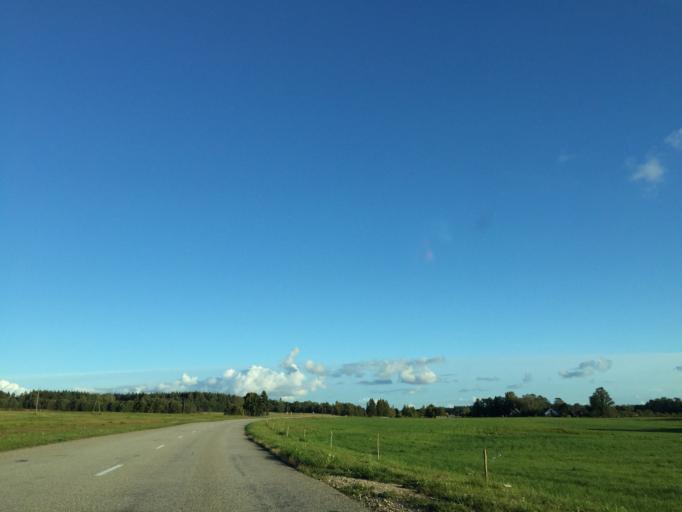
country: LV
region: Kuldigas Rajons
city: Kuldiga
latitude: 56.9278
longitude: 22.0479
